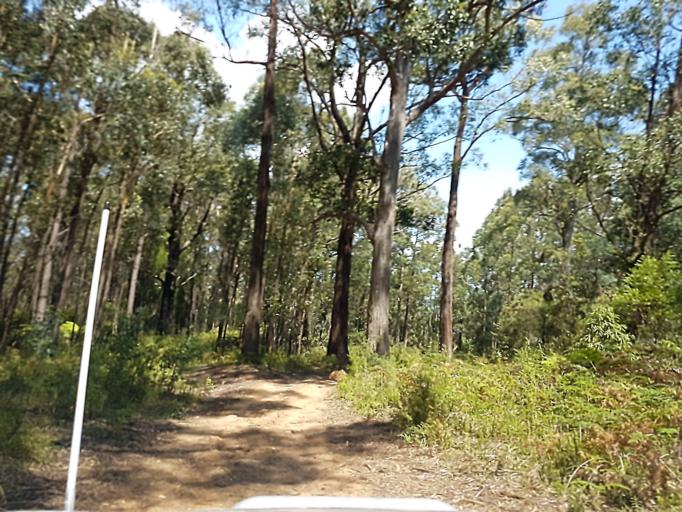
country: AU
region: Victoria
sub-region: East Gippsland
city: Lakes Entrance
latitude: -37.3931
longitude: 148.2957
